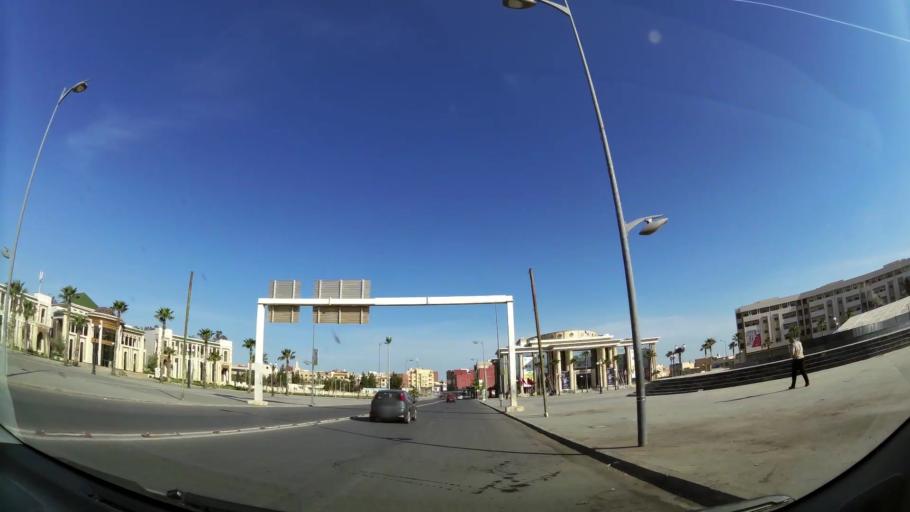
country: MA
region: Oriental
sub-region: Oujda-Angad
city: Oujda
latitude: 34.6774
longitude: -1.9293
